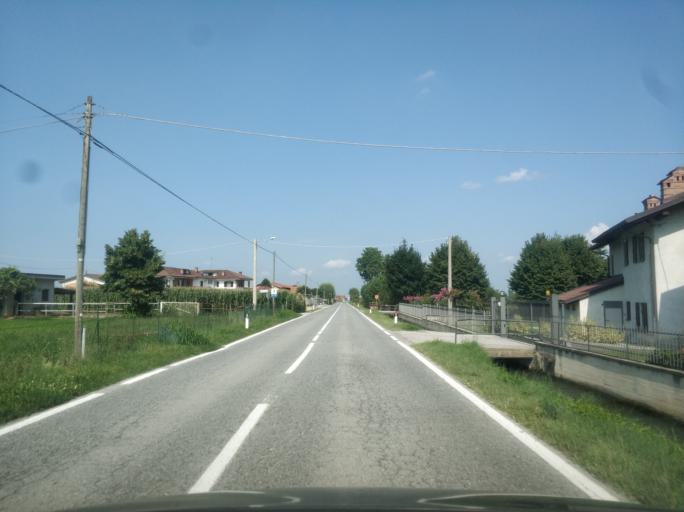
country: IT
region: Piedmont
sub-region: Provincia di Cuneo
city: Roata Rossi
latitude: 44.4663
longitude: 7.5036
